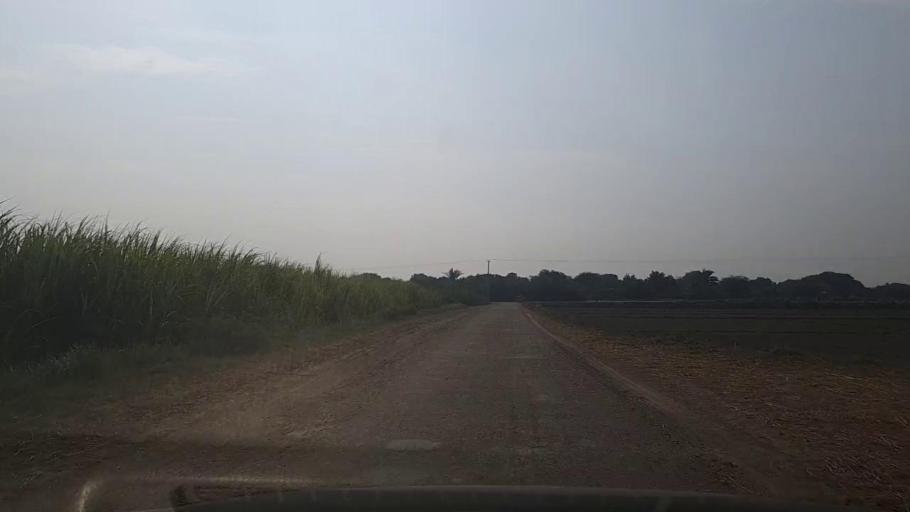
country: PK
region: Sindh
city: Bulri
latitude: 25.0089
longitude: 68.3000
